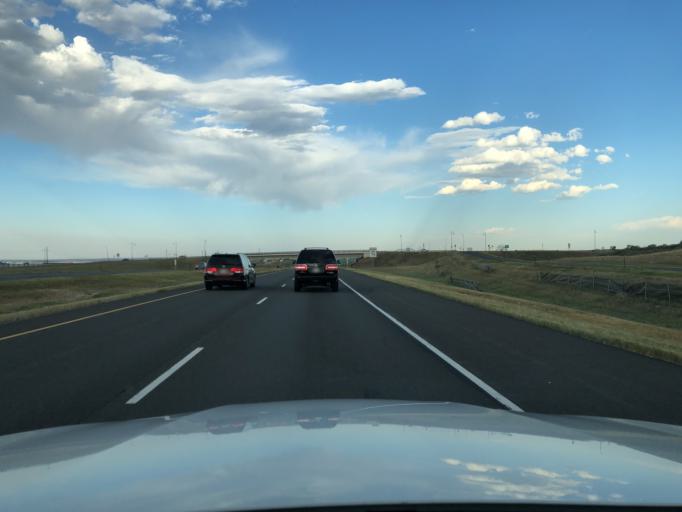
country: US
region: Colorado
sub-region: Boulder County
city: Lafayette
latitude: 39.9838
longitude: -105.0227
